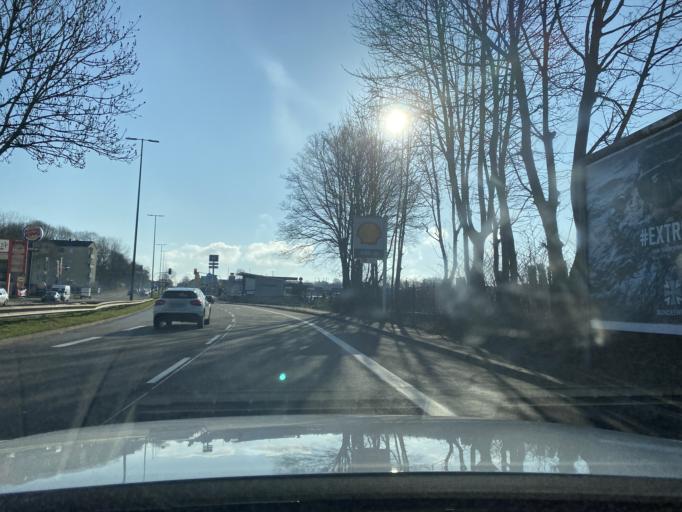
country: DE
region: North Rhine-Westphalia
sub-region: Regierungsbezirk Dusseldorf
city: Remscheid
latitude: 51.1775
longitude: 7.2090
